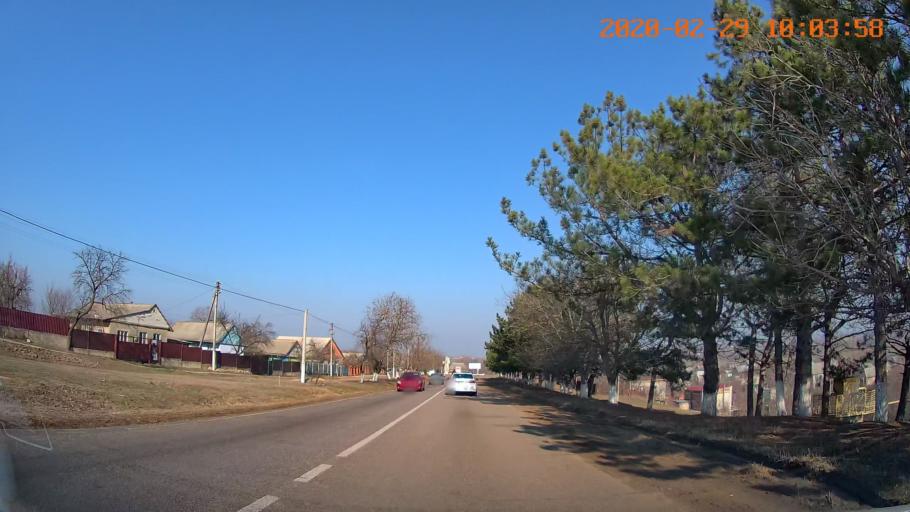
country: MD
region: Causeni
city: Chitcani
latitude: 46.7945
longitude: 29.6779
